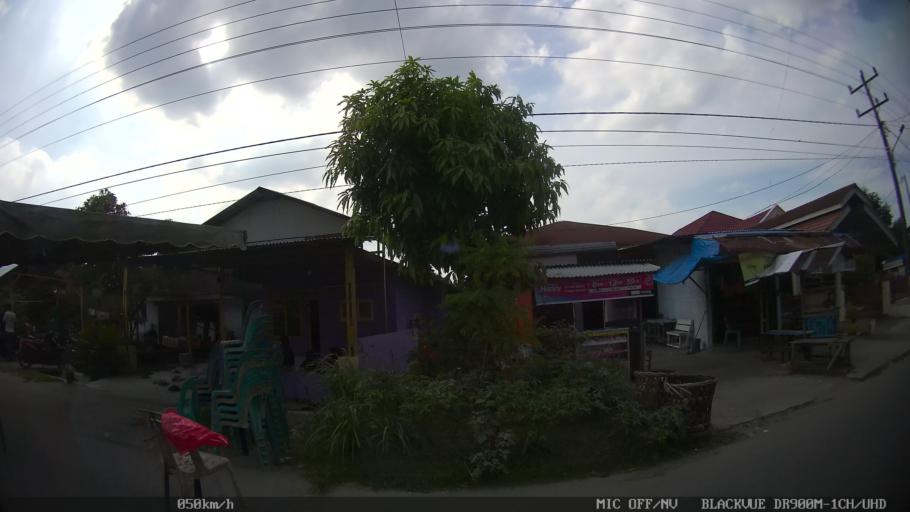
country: ID
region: North Sumatra
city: Binjai
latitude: 3.6382
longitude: 98.4927
